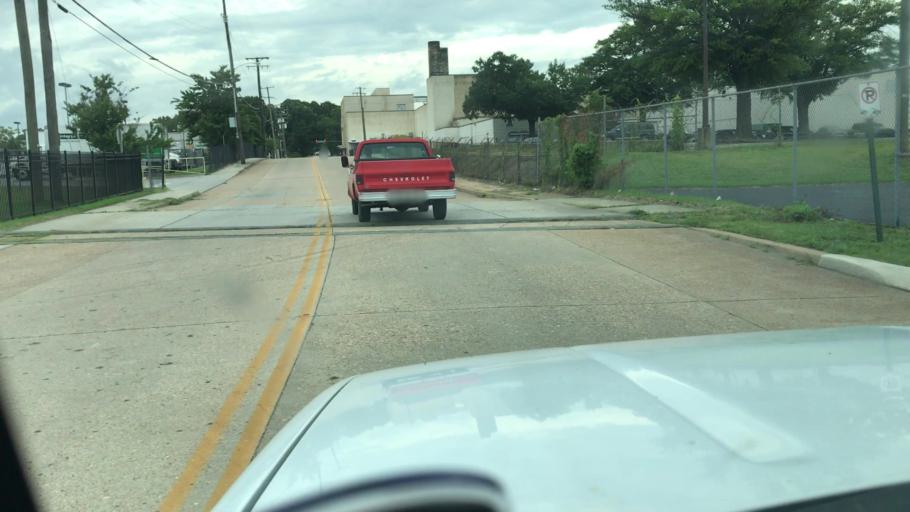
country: US
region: Virginia
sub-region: City of Richmond
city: Richmond
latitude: 37.5574
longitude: -77.4569
